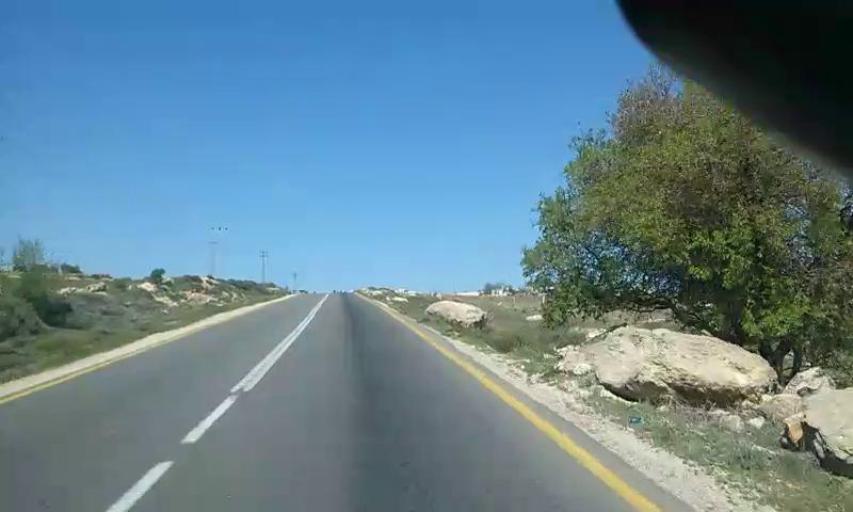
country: PS
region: West Bank
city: Marah Rabbah
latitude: 31.6466
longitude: 35.1880
